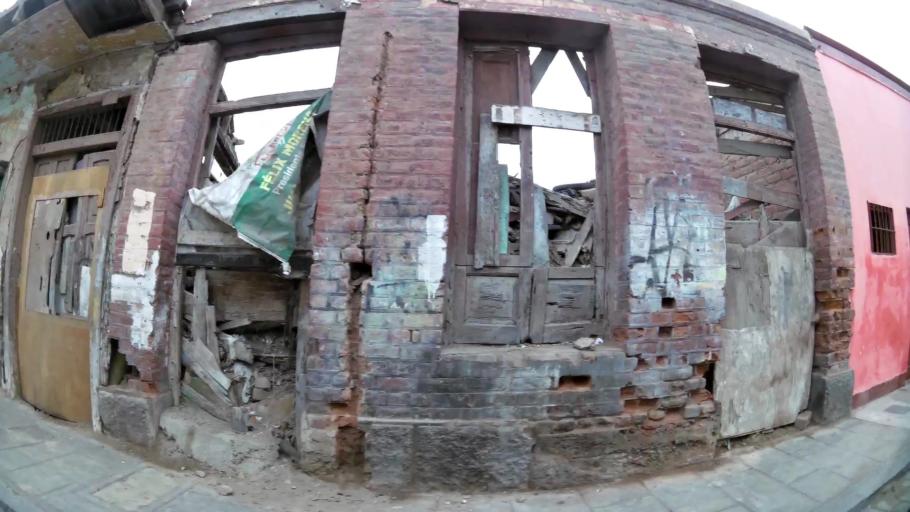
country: PE
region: Callao
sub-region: Callao
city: Callao
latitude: -12.0601
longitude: -77.1450
